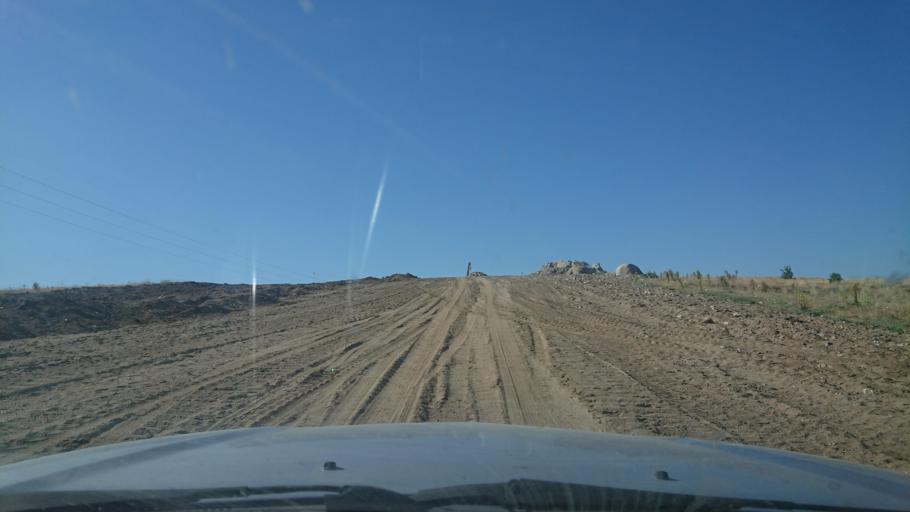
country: TR
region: Aksaray
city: Agacoren
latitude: 38.8446
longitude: 33.9438
